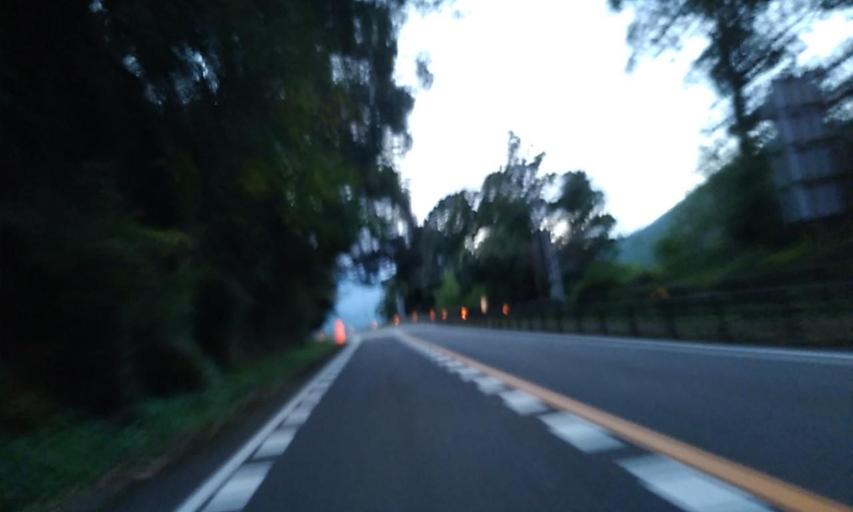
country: JP
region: Wakayama
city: Shingu
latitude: 33.7232
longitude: 135.9657
